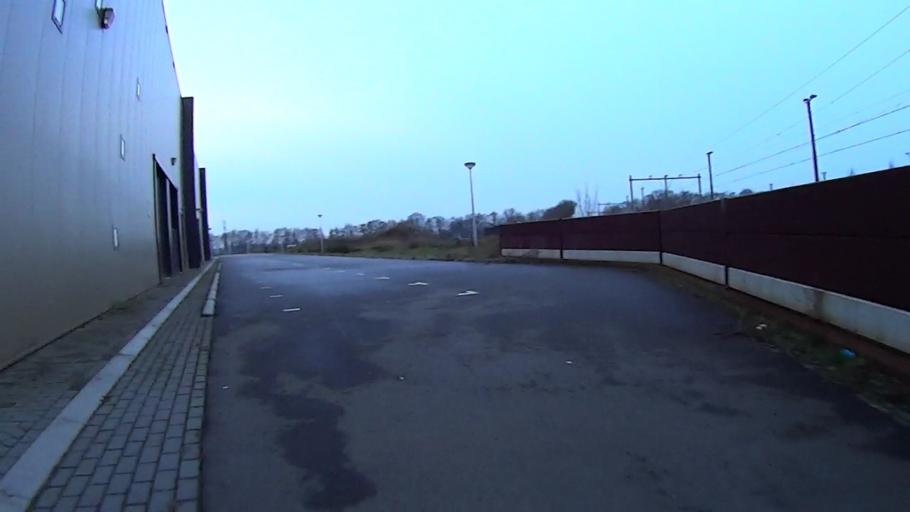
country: NL
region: Utrecht
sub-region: Gemeente Amersfoort
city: Hoogland
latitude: 52.1621
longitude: 5.3465
